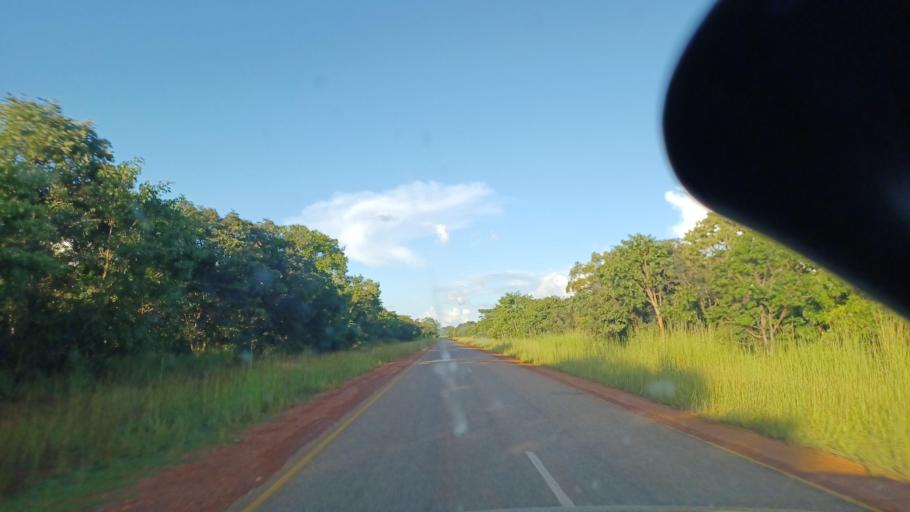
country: ZM
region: North-Western
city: Kalengwa
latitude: -13.1433
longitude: 25.0590
